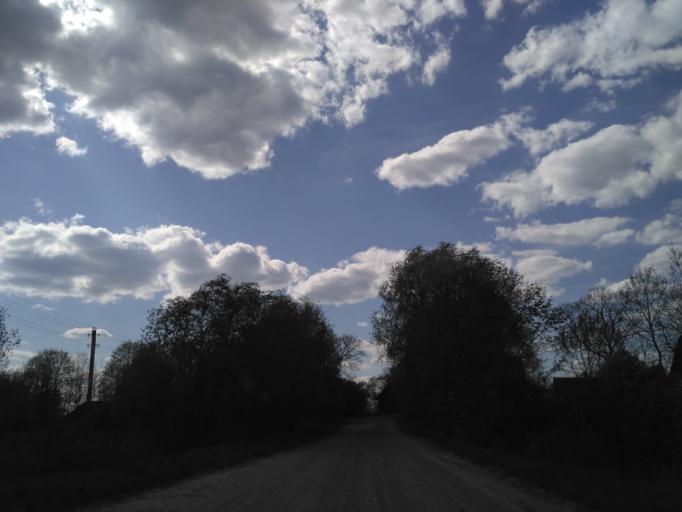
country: BY
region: Minsk
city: Narach
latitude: 54.9912
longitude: 26.5856
